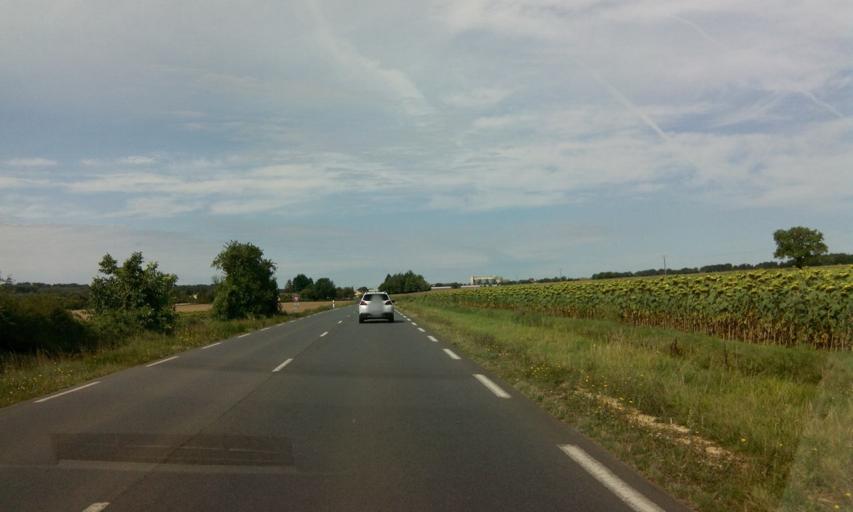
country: FR
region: Poitou-Charentes
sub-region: Departement des Deux-Sevres
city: Sauze-Vaussais
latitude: 46.1359
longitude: 0.1475
